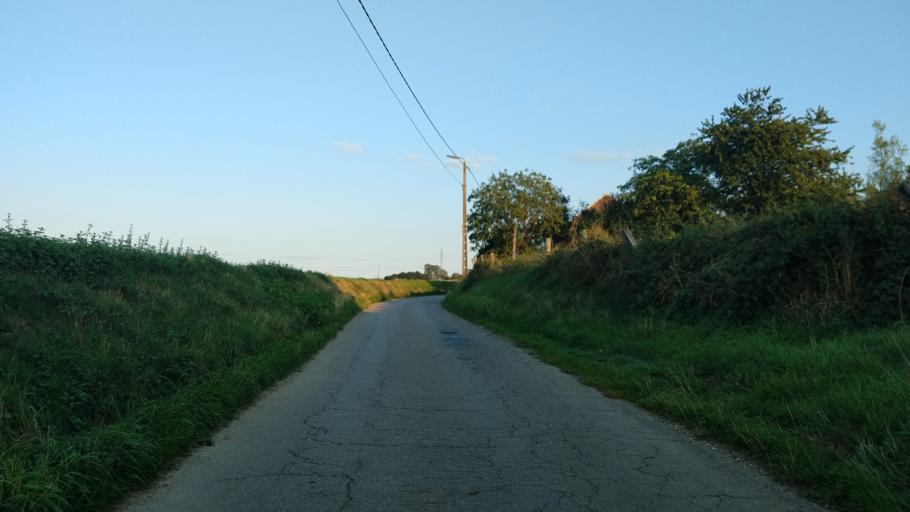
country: BE
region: Flanders
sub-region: Provincie Vlaams-Brabant
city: Lubbeek
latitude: 50.8807
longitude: 4.7926
